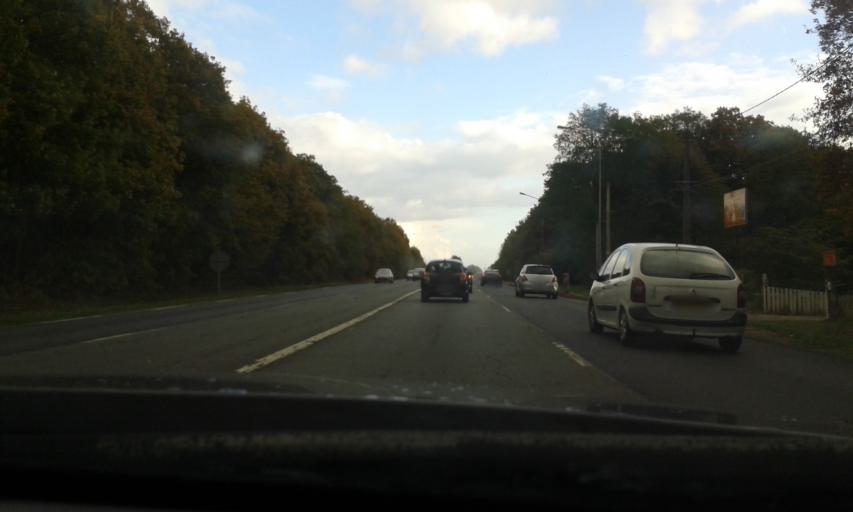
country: FR
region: Centre
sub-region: Departement d'Eure-et-Loir
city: Saint-Remy-sur-Avre
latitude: 48.7536
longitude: 1.2551
